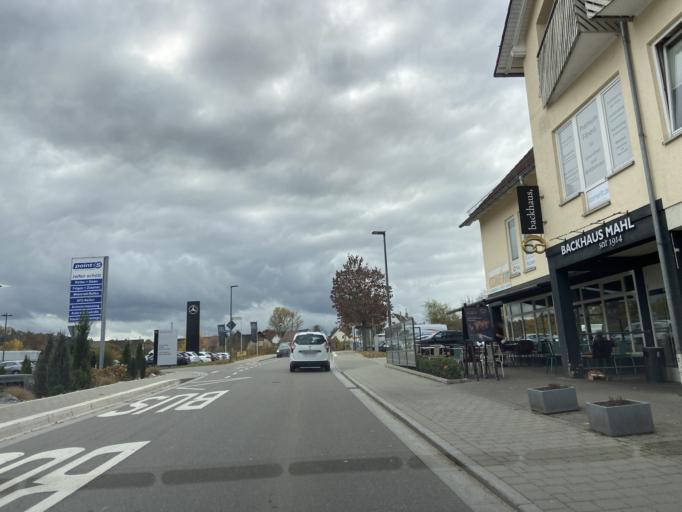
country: DE
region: Baden-Wuerttemberg
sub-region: Tuebingen Region
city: Inzigkofen
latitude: 48.0772
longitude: 9.1952
